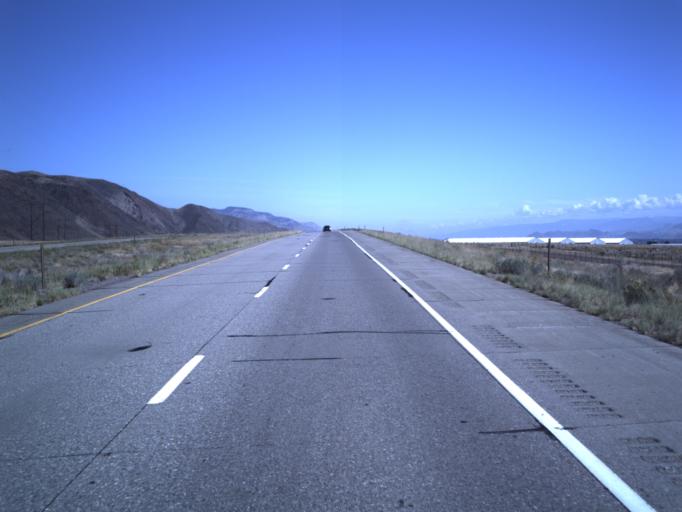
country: US
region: Utah
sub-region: Sevier County
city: Monroe
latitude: 38.7045
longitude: -112.1407
